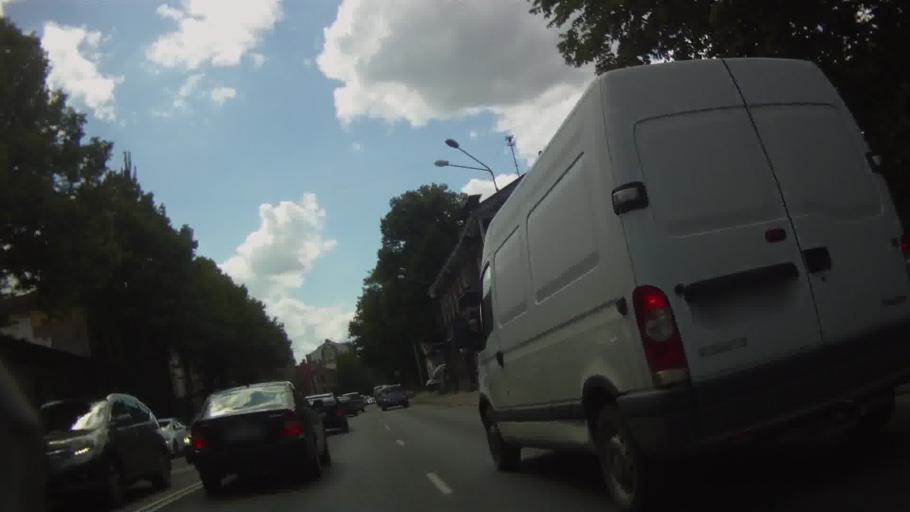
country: LV
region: Riga
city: Riga
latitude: 56.9430
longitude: 24.0670
